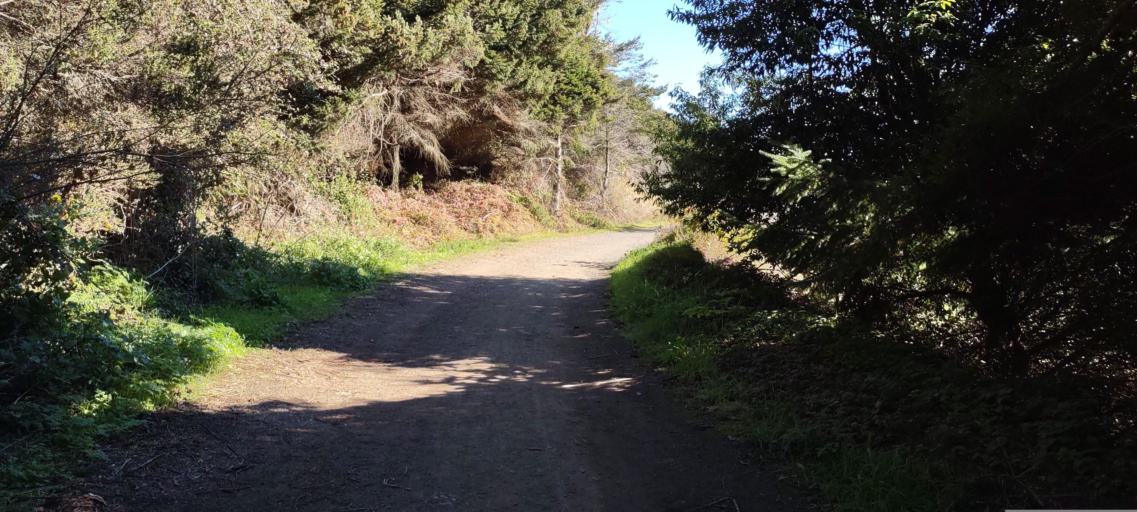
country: US
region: California
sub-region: Mendocino County
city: Fort Bragg
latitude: 39.3043
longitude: -123.7825
